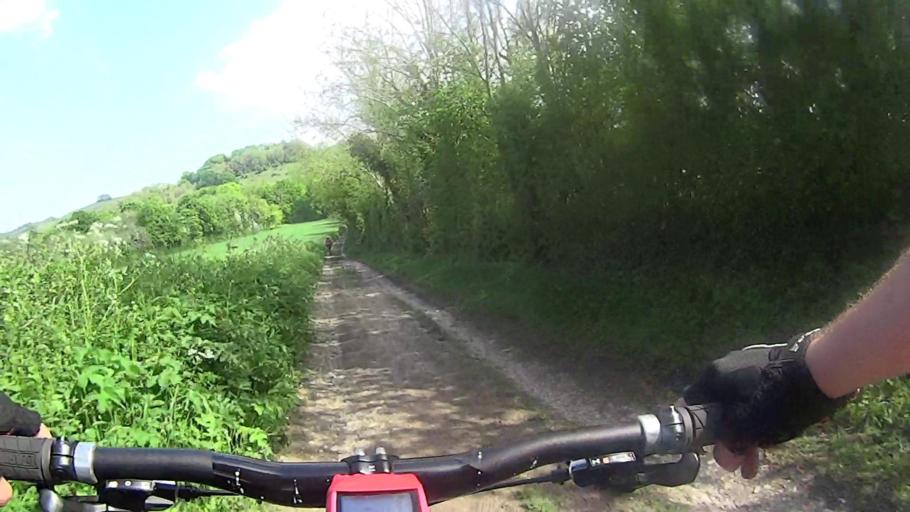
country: GB
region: England
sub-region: Hampshire
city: Petersfield
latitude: 50.9614
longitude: -0.8898
